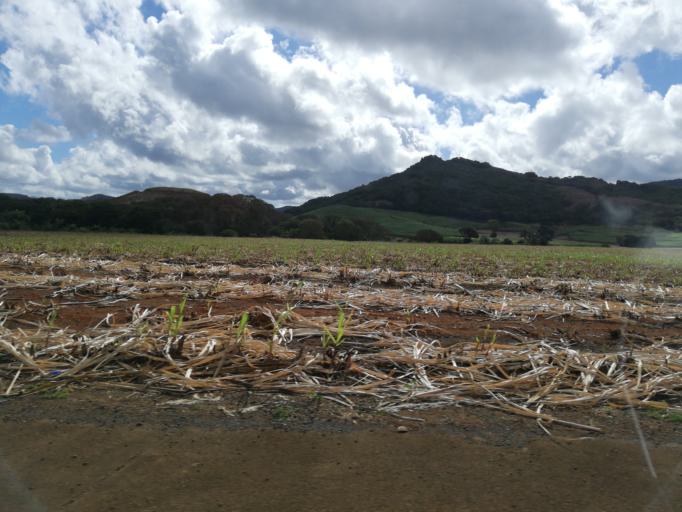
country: MU
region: Grand Port
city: Bois des Amourettes
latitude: -20.3671
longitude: 57.7032
